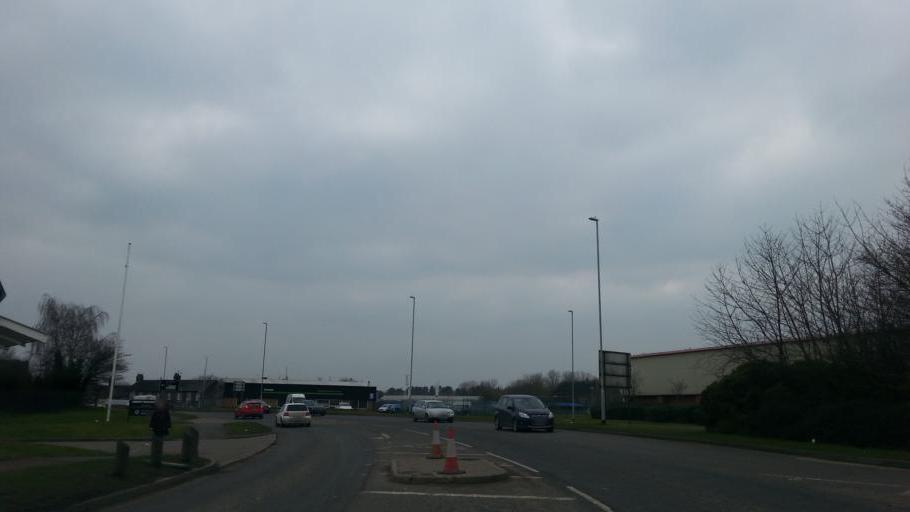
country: GB
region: England
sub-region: Northamptonshire
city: Corby
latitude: 52.4942
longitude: -0.6808
